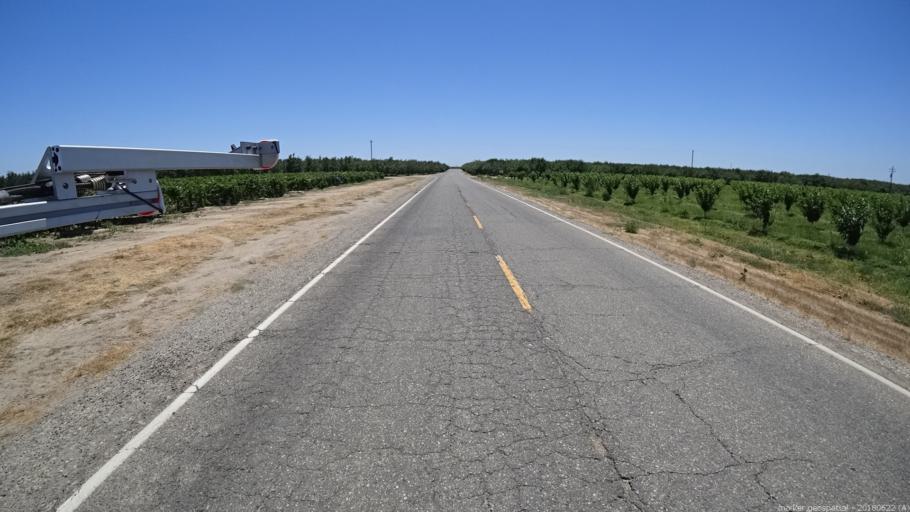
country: US
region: California
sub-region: Madera County
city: Parksdale
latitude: 36.9030
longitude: -119.9924
